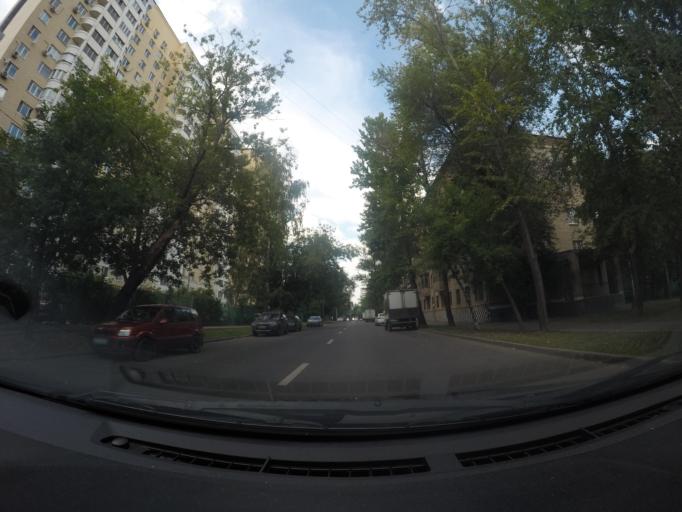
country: RU
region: Moscow
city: Kozeyevo
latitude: 55.8549
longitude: 37.6090
